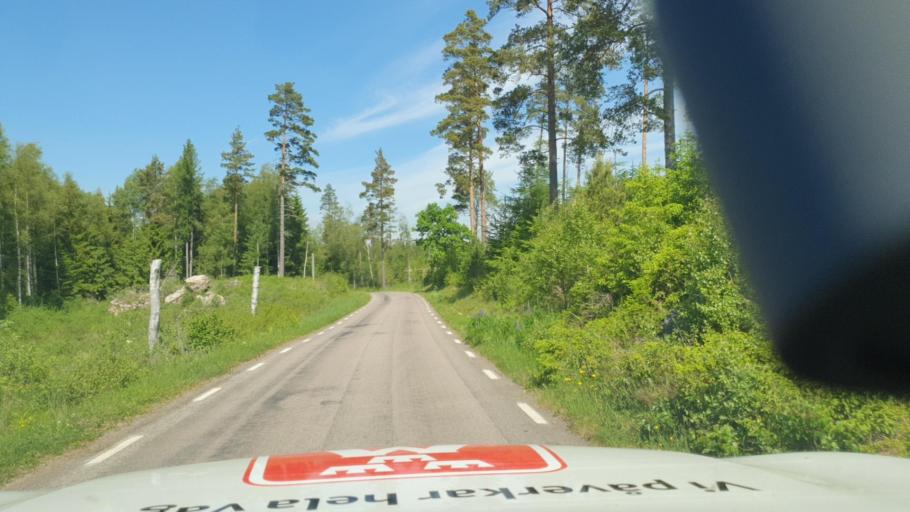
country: SE
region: Vaestra Goetaland
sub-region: Herrljunga Kommun
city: Herrljunga
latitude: 58.1322
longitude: 13.0837
